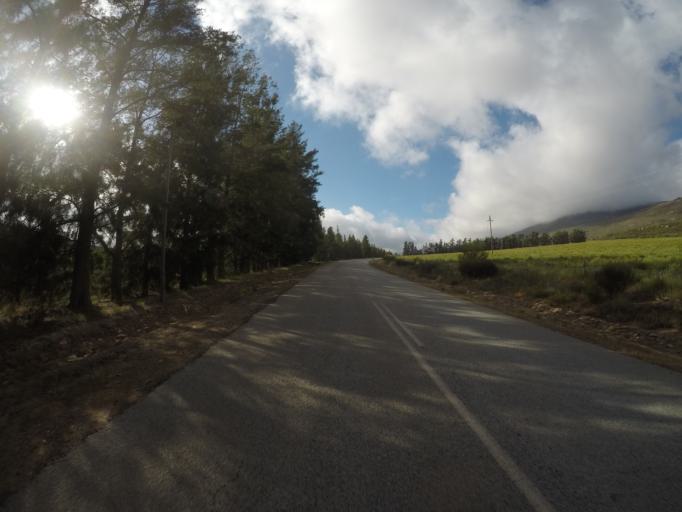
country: ZA
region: Western Cape
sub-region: West Coast District Municipality
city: Clanwilliam
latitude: -32.3482
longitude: 18.8454
